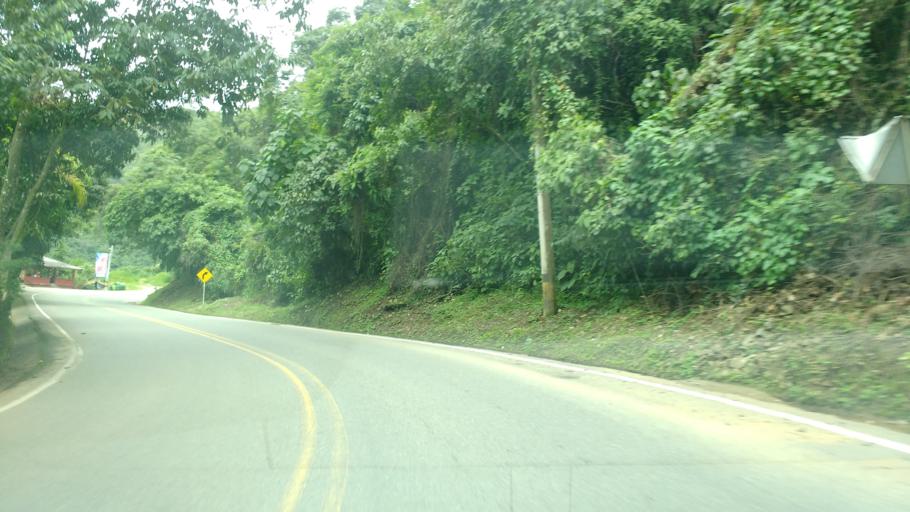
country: CO
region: Antioquia
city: Amaga
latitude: 6.0590
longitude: -75.7390
